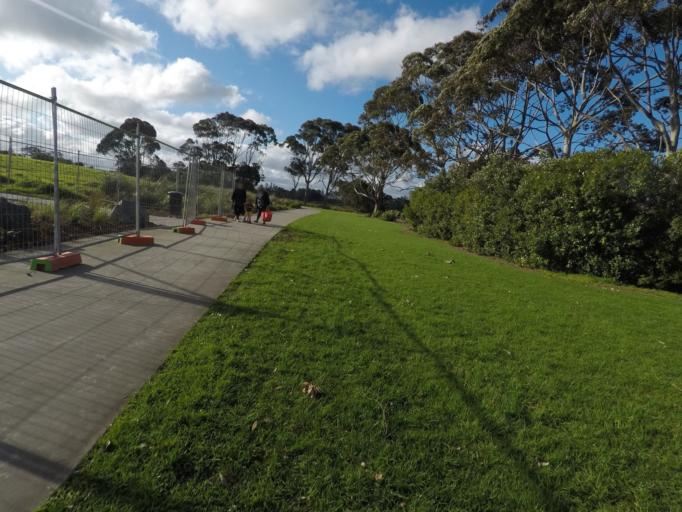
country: NZ
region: Auckland
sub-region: Auckland
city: Rosebank
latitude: -36.8937
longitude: 174.6715
